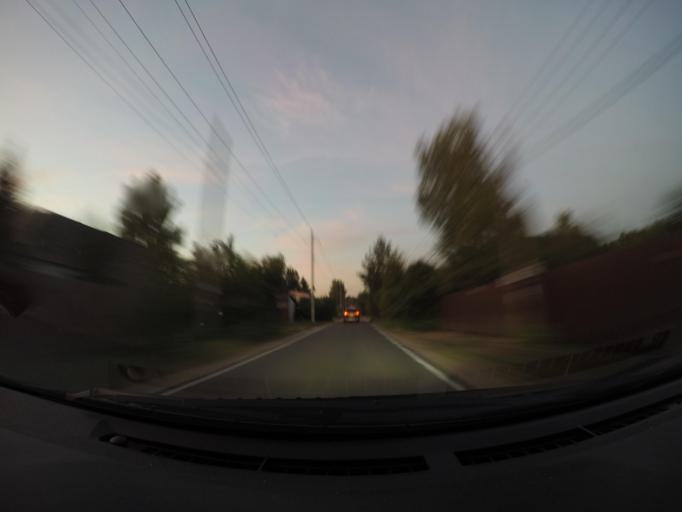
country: RU
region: Moskovskaya
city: Rechitsy
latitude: 55.5491
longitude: 38.4600
